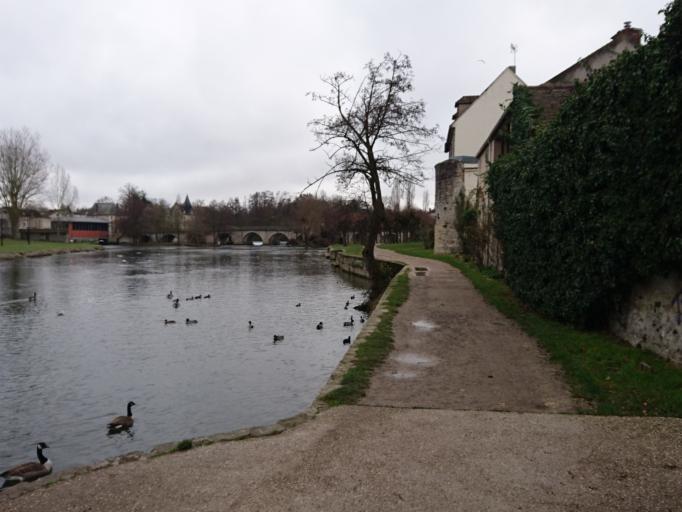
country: FR
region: Ile-de-France
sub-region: Departement de Seine-et-Marne
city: Moret-sur-Loing
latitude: 48.3745
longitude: 2.8179
